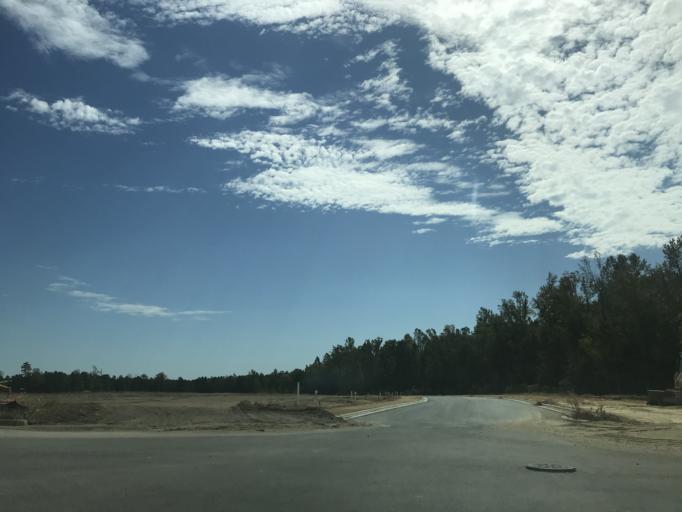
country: US
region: North Carolina
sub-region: Wake County
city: Knightdale
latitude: 35.8596
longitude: -78.5394
